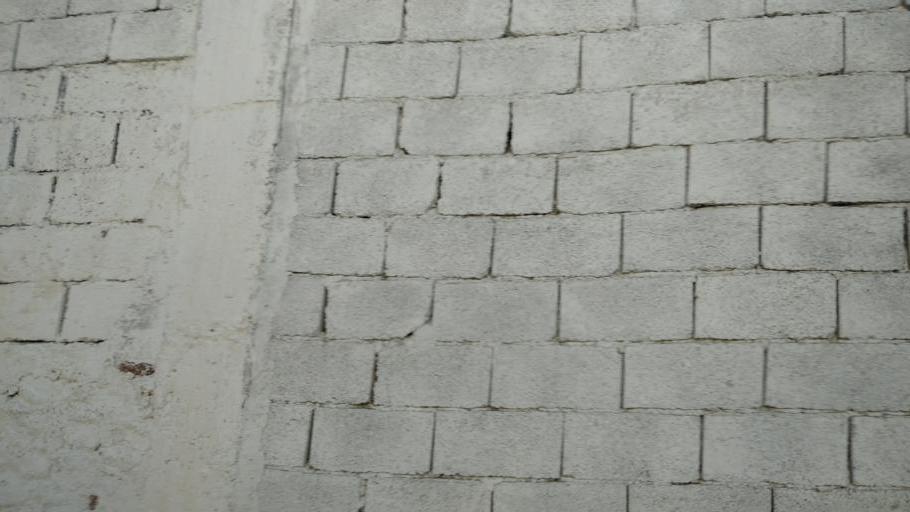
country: AL
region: Shkoder
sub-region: Rrethi i Shkodres
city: Shkoder
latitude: 42.0771
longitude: 19.5054
